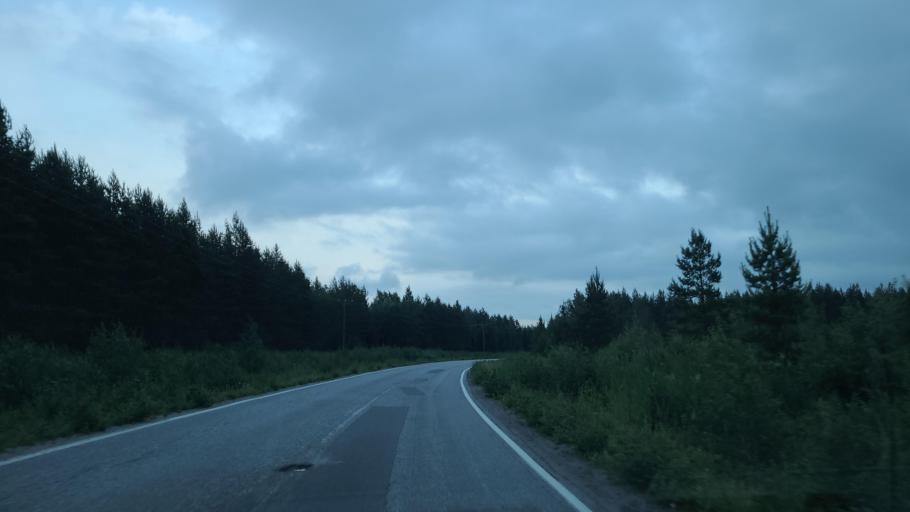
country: FI
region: Ostrobothnia
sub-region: Vaasa
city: Replot
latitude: 63.2221
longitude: 21.2439
